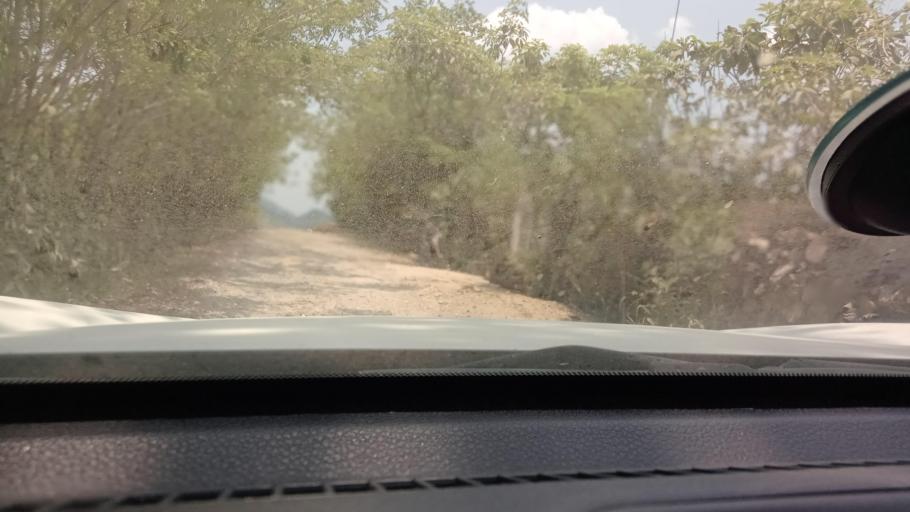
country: MX
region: Tabasco
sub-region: Huimanguillo
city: Francisco Rueda
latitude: 17.5114
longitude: -93.8967
